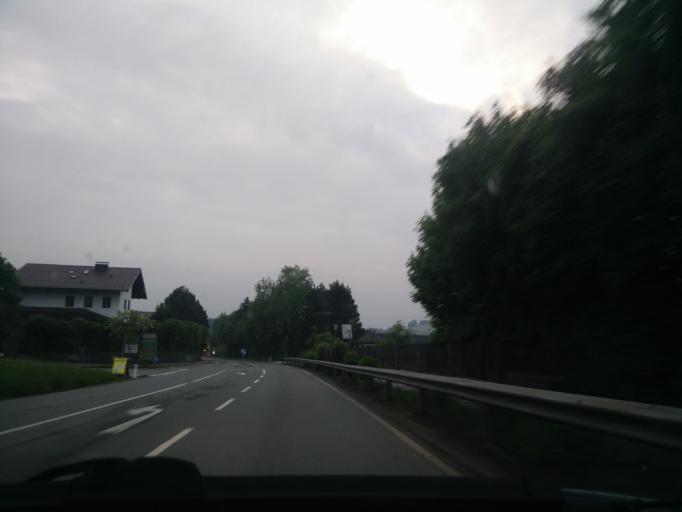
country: AT
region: Salzburg
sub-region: Politischer Bezirk Salzburg-Umgebung
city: Elixhausen
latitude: 47.8648
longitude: 13.0633
